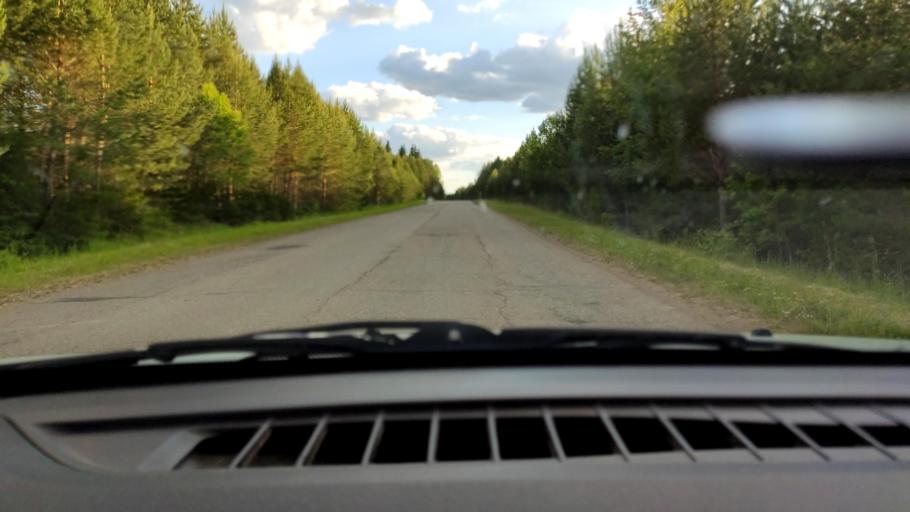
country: RU
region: Perm
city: Uinskoye
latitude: 57.0878
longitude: 56.6268
